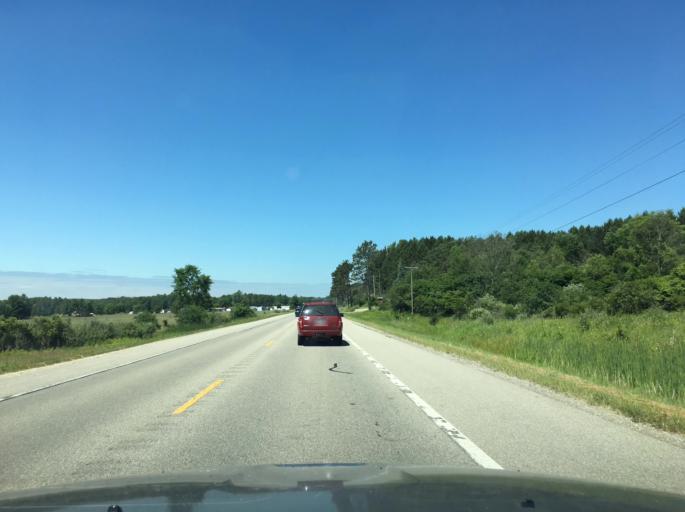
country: US
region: Michigan
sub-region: Osceola County
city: Reed City
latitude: 43.8729
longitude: -85.4667
